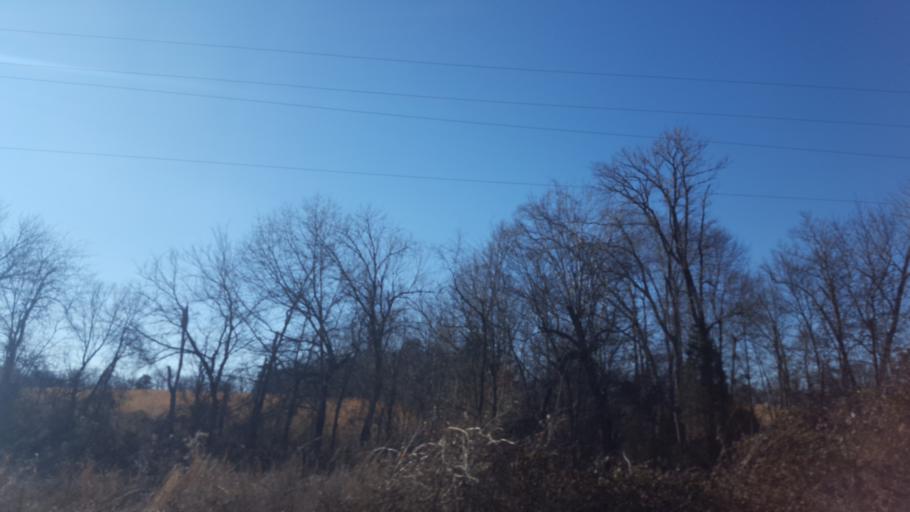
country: US
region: Kentucky
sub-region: Crittenden County
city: Marion
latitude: 37.4268
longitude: -88.0453
